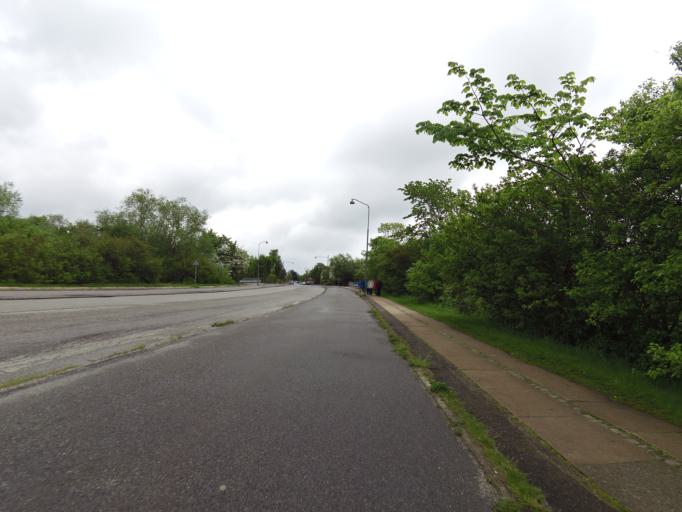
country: DK
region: Capital Region
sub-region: Frederiksberg Kommune
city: Frederiksberg
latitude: 55.7225
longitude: 12.5213
